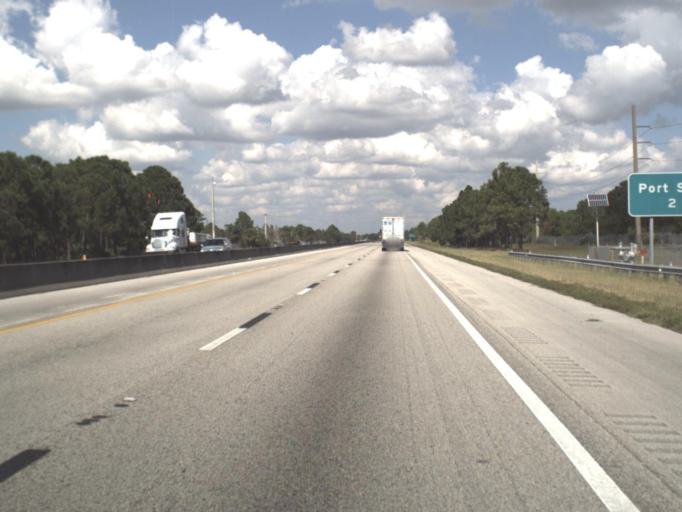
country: US
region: Florida
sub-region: Saint Lucie County
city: Port Saint Lucie
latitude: 27.2458
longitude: -80.3465
